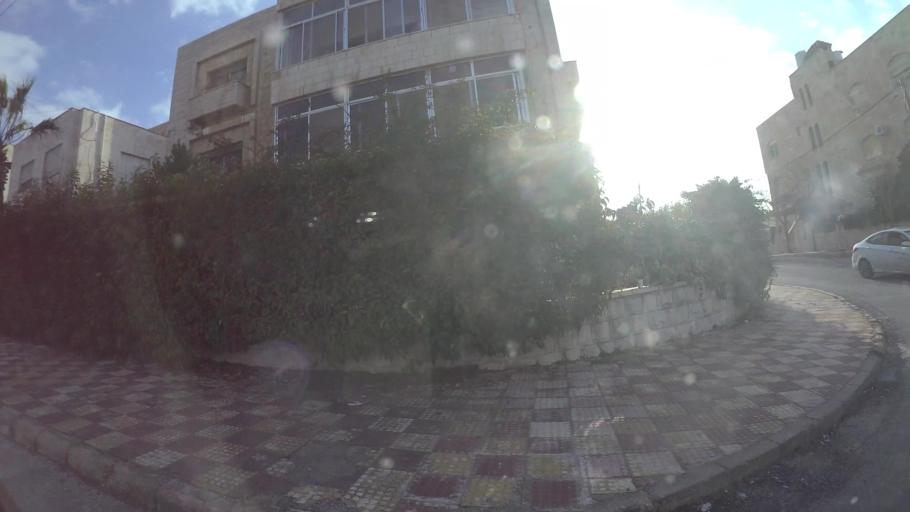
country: JO
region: Amman
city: Al Jubayhah
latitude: 32.0080
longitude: 35.8655
